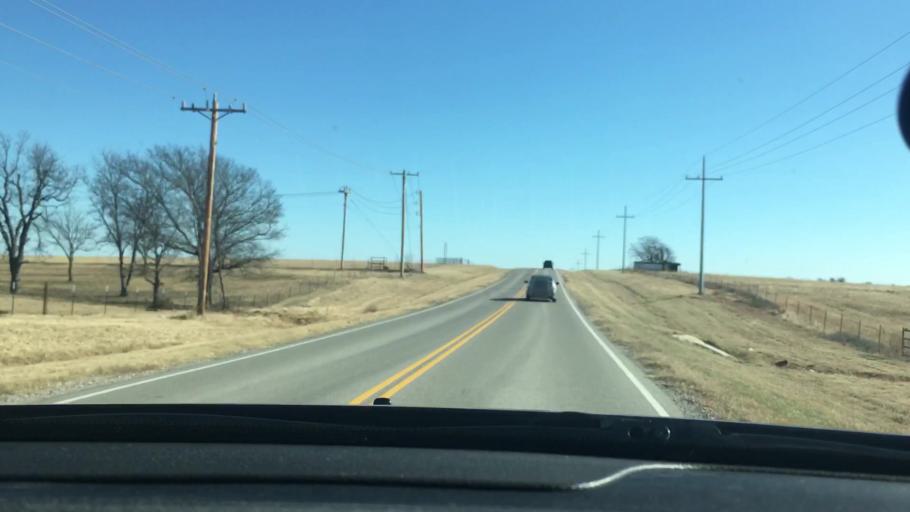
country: US
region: Oklahoma
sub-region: Murray County
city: Davis
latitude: 34.4773
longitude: -97.1007
